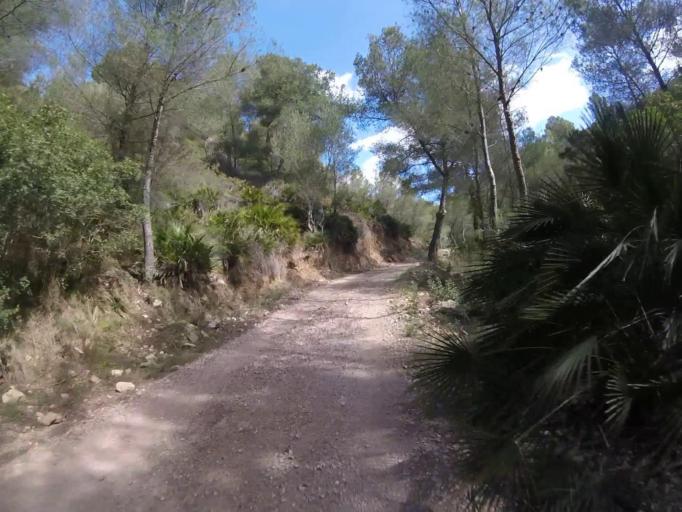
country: ES
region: Valencia
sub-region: Provincia de Castello
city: Alcoceber
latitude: 40.2993
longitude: 0.3149
